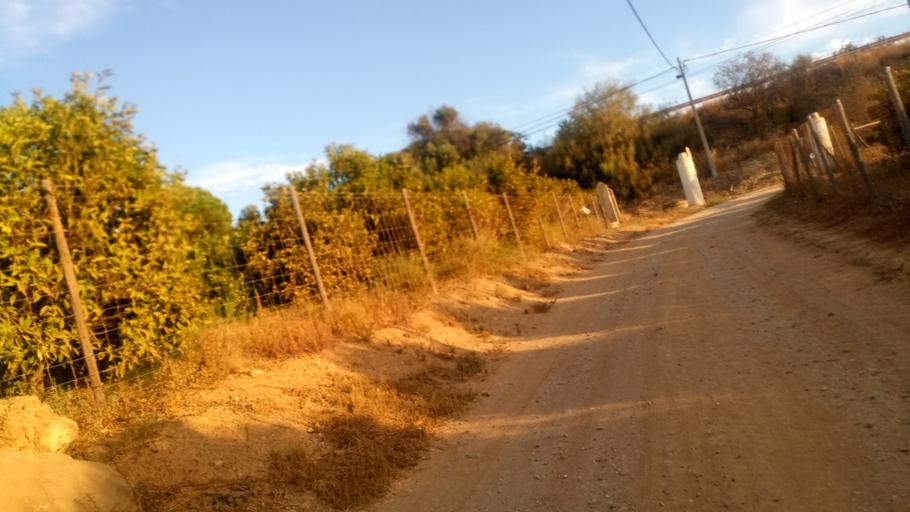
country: PT
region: Faro
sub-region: Tavira
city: Tavira
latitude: 37.1527
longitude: -7.5869
